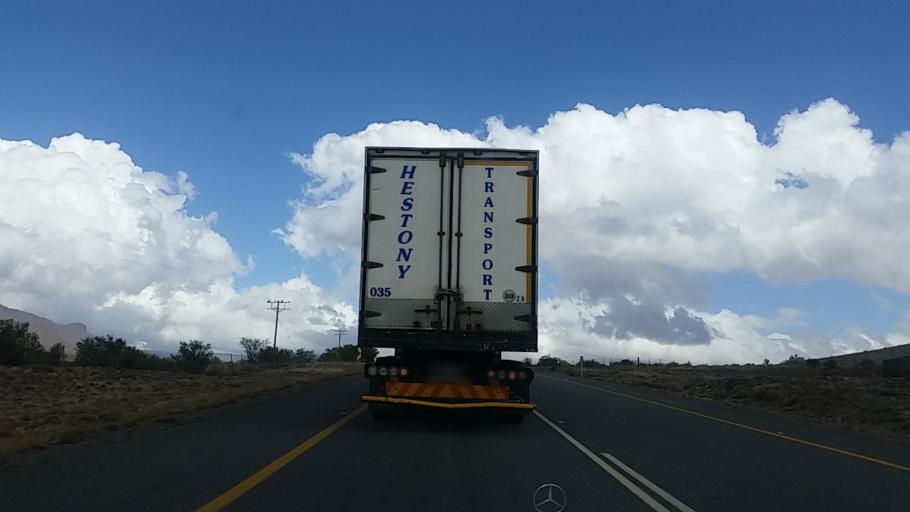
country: ZA
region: Eastern Cape
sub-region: Chris Hani District Municipality
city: Middelburg
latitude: -31.7316
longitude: 24.9456
